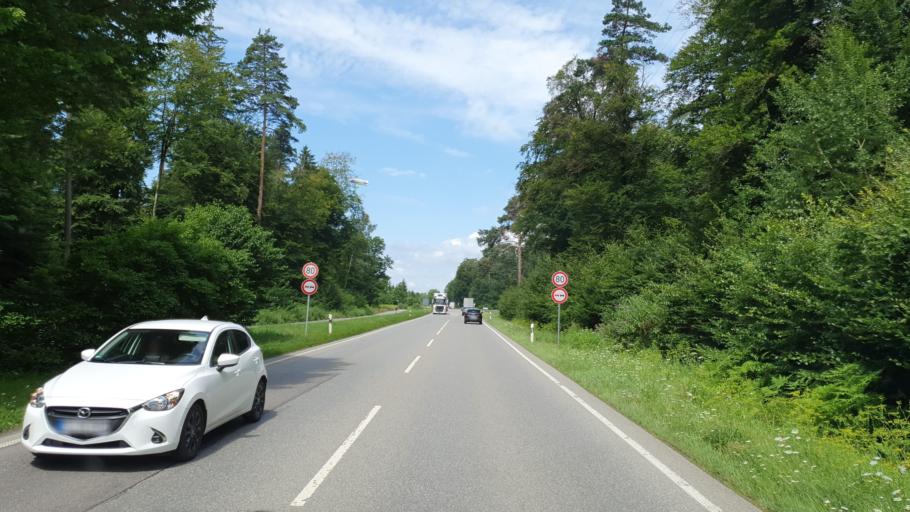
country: DE
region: Baden-Wuerttemberg
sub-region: Tuebingen Region
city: Eriskirch
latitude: 47.6225
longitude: 9.5570
